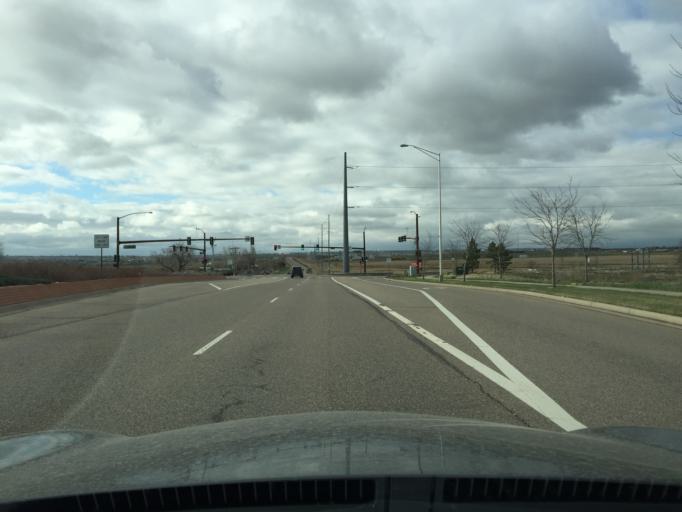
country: US
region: Colorado
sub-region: Boulder County
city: Erie
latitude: 39.9877
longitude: -104.9785
